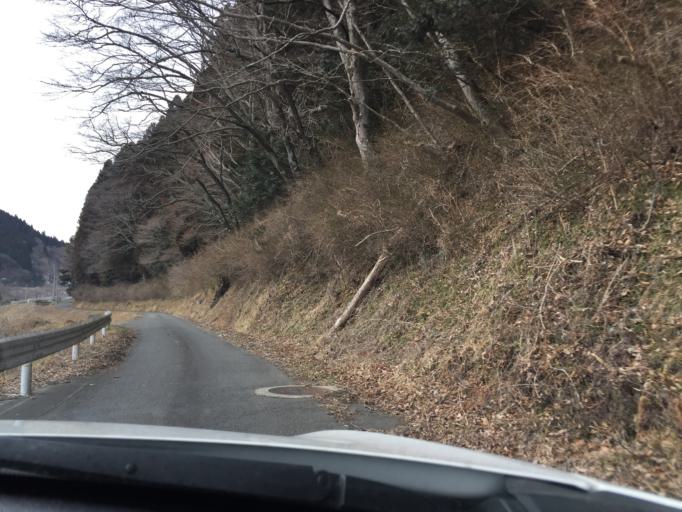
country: JP
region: Fukushima
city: Ishikawa
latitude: 37.1483
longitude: 140.6715
